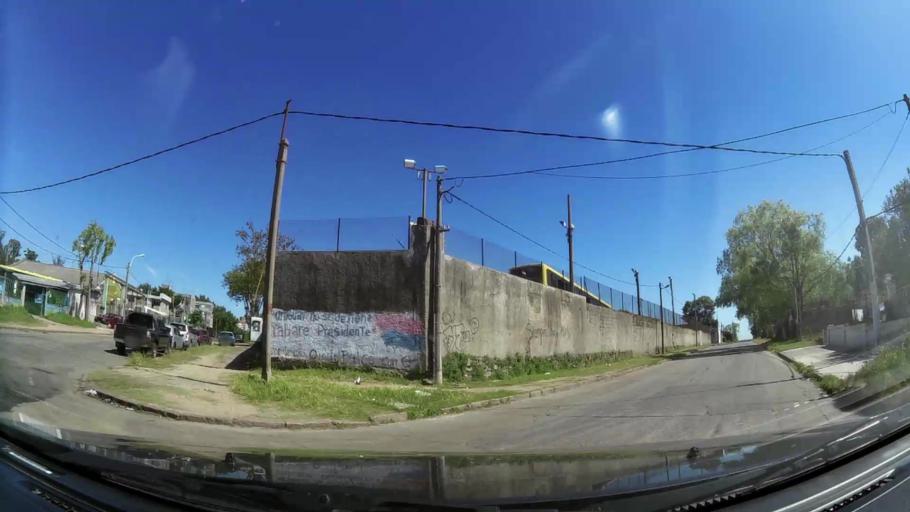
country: UY
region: Montevideo
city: Montevideo
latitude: -34.8696
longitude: -56.1290
